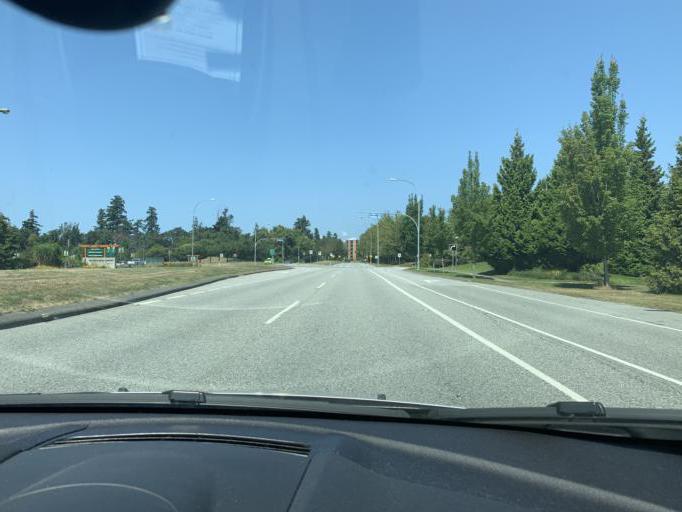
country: CA
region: British Columbia
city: West End
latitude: 49.2538
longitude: -123.2489
